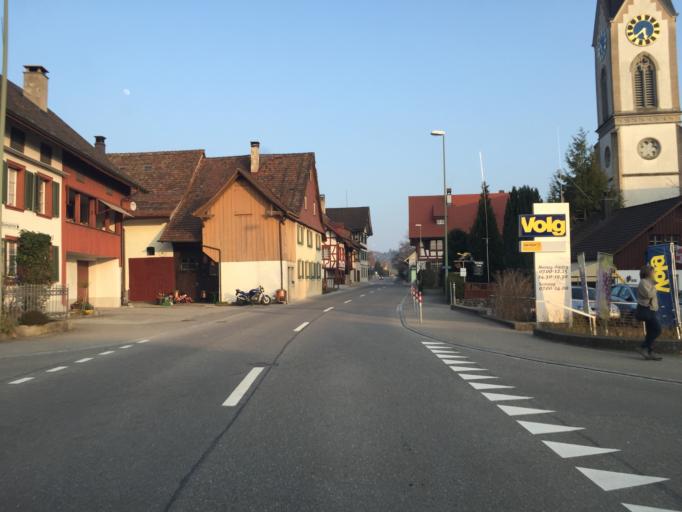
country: CH
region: Zurich
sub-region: Bezirk Andelfingen
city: Marthalen
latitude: 47.6531
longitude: 8.6535
